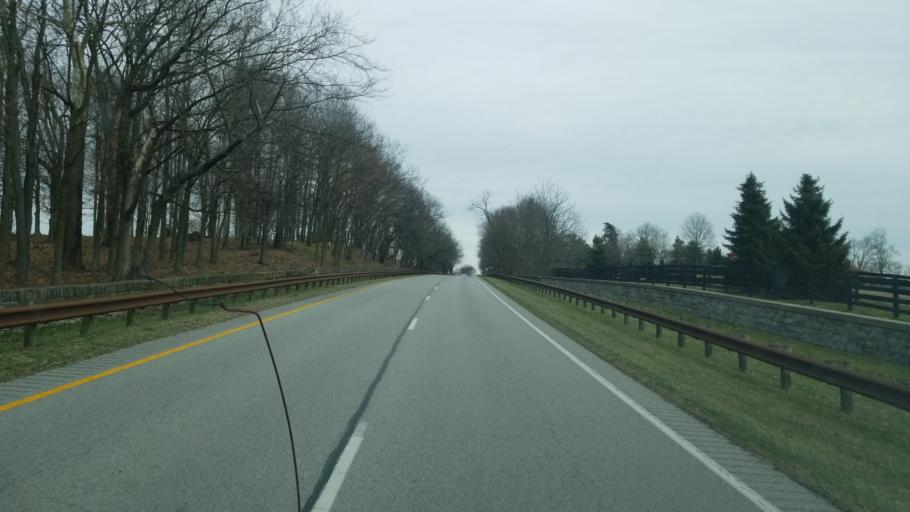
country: US
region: Kentucky
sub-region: Fayette County
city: Lexington-Fayette
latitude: 38.1098
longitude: -84.4039
